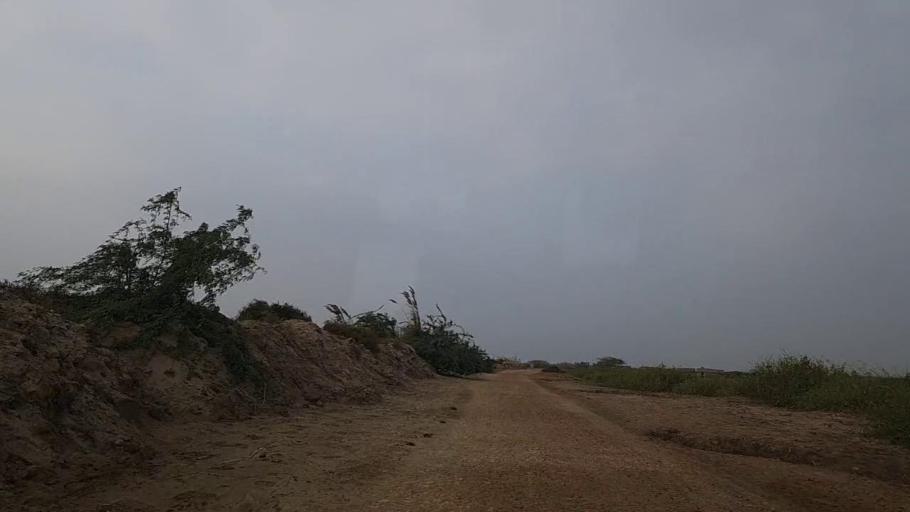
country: PK
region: Sindh
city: Mirpur Sakro
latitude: 24.6094
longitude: 67.5156
